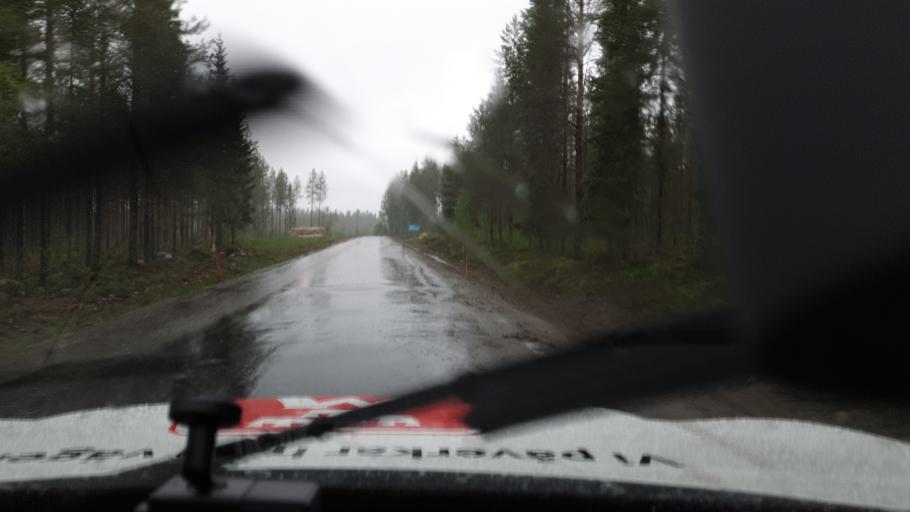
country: SE
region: Vaesterbotten
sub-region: Umea Kommun
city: Roback
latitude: 64.0158
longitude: 20.0807
